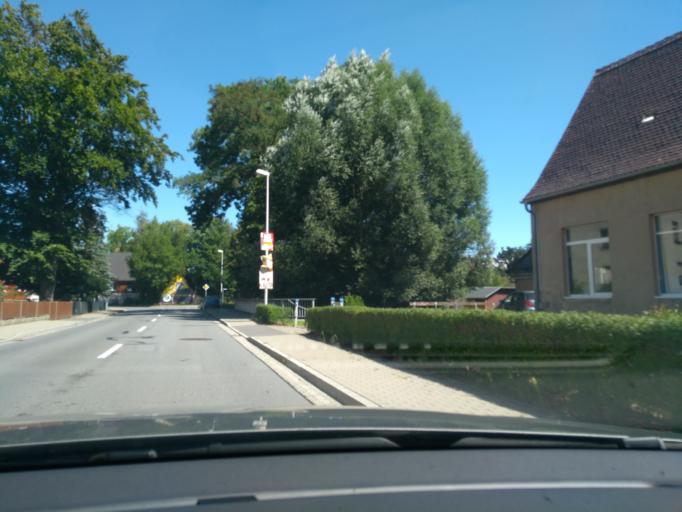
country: DE
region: Saxony
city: Grossrohrsdorf
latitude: 51.1388
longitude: 14.0021
